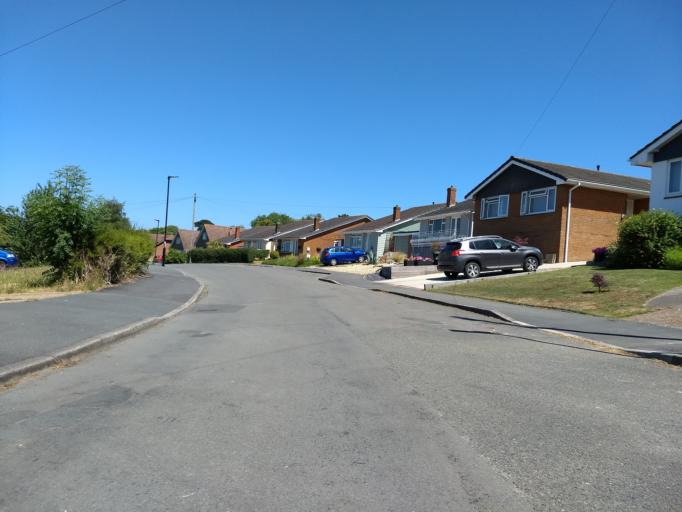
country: GB
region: England
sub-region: Isle of Wight
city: Seaview
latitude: 50.7100
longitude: -1.1103
